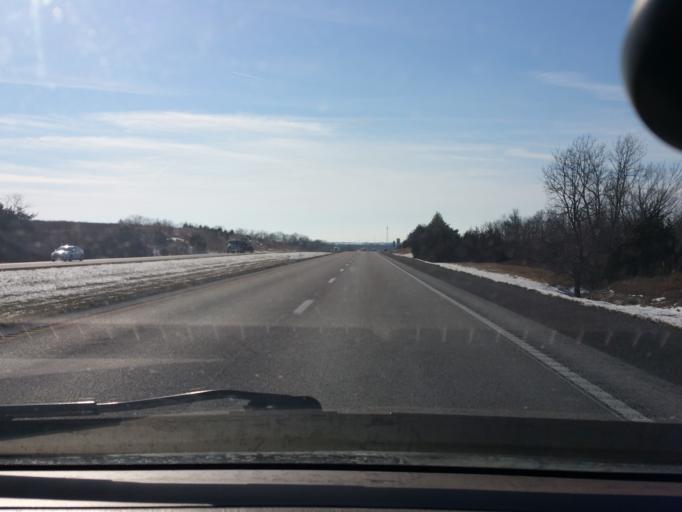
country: US
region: Missouri
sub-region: Clinton County
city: Cameron
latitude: 39.8938
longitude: -94.1548
